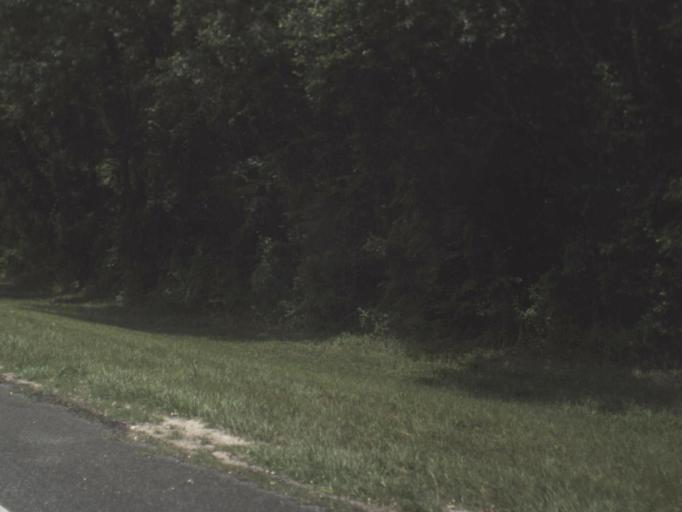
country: US
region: Florida
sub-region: Suwannee County
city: Live Oak
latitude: 30.1730
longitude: -82.9781
